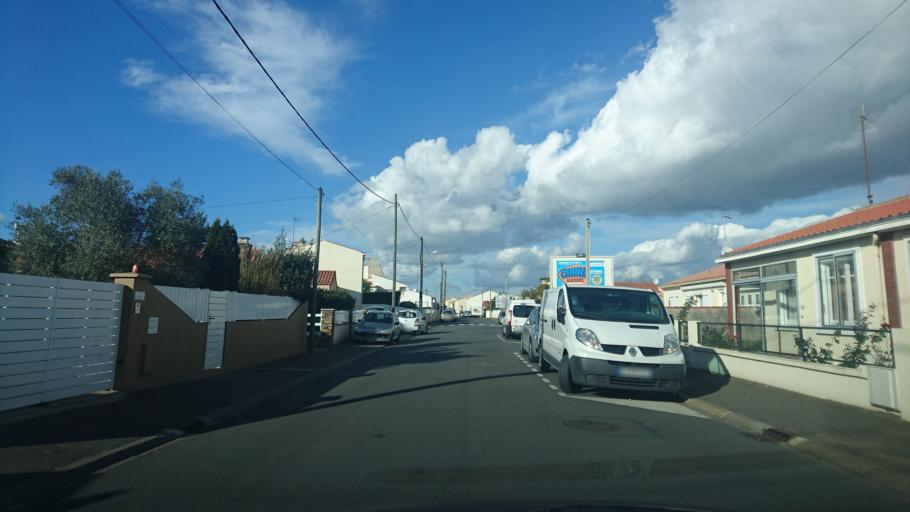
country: FR
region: Pays de la Loire
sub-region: Departement de la Vendee
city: Les Sables-d'Olonne
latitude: 46.5046
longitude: -1.8002
